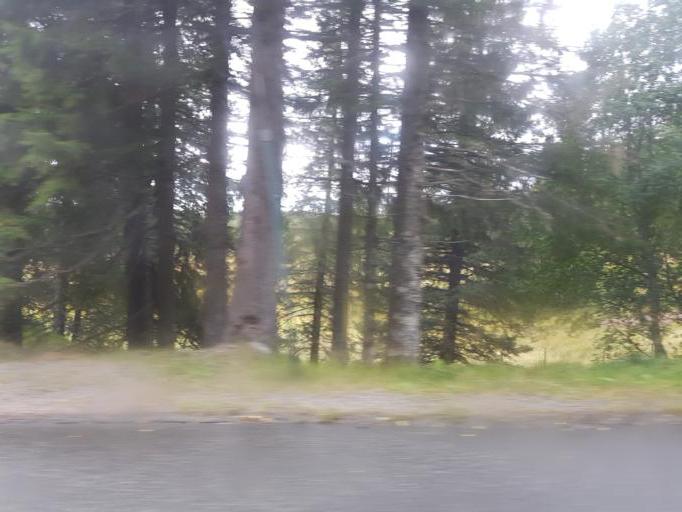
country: NO
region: Sor-Trondelag
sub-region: Melhus
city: Melhus
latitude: 63.4166
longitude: 10.2638
